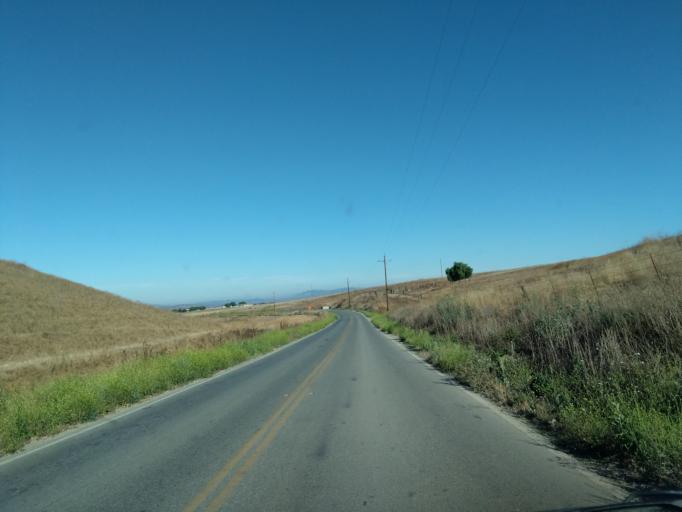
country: US
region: California
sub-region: San Benito County
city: Ridgemark
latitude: 36.8269
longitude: -121.3329
